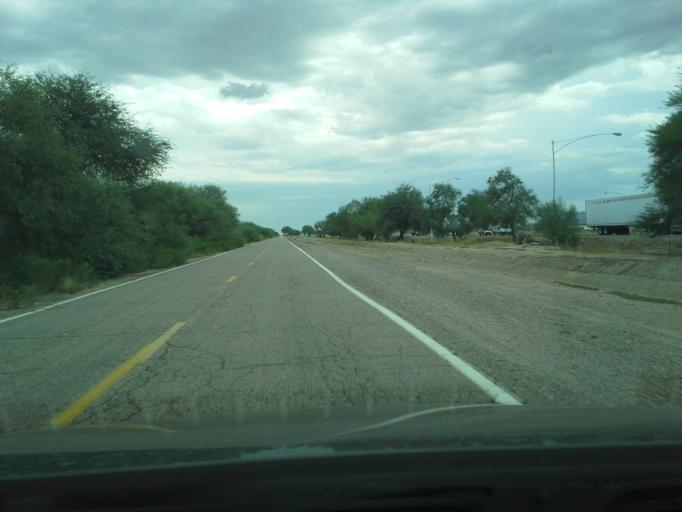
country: US
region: Arizona
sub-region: Pima County
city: Marana
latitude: 32.4672
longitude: -111.2225
